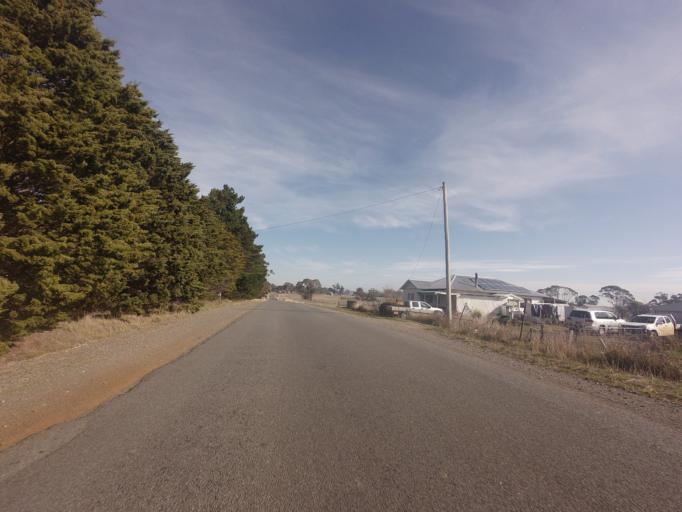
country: AU
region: Tasmania
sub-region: Sorell
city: Sorell
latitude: -42.4427
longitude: 147.4692
